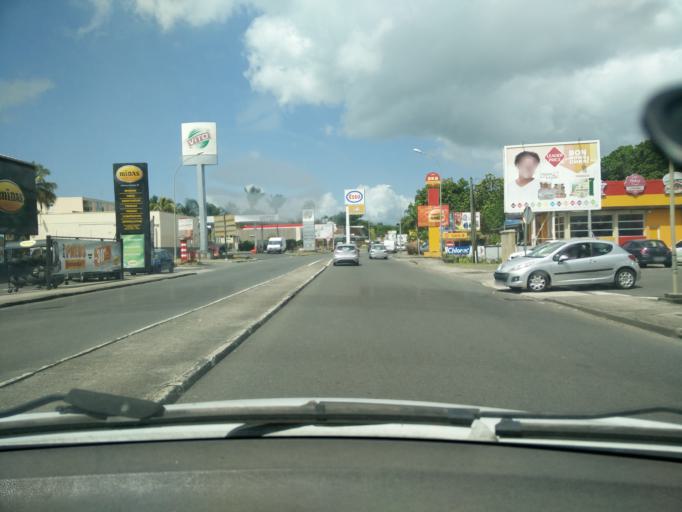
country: GP
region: Guadeloupe
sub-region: Guadeloupe
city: Pointe-a-Pitre
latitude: 16.2532
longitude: -61.5241
